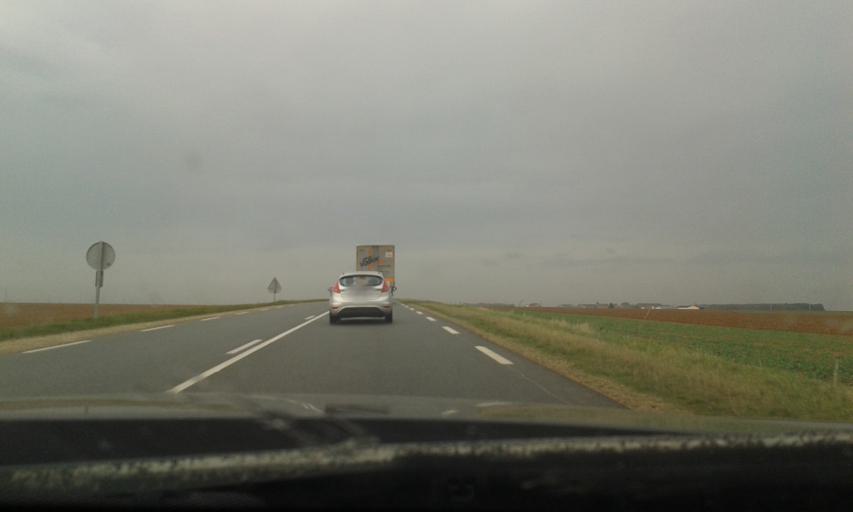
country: FR
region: Centre
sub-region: Departement d'Eure-et-Loir
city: Janville
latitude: 48.2304
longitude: 1.7929
